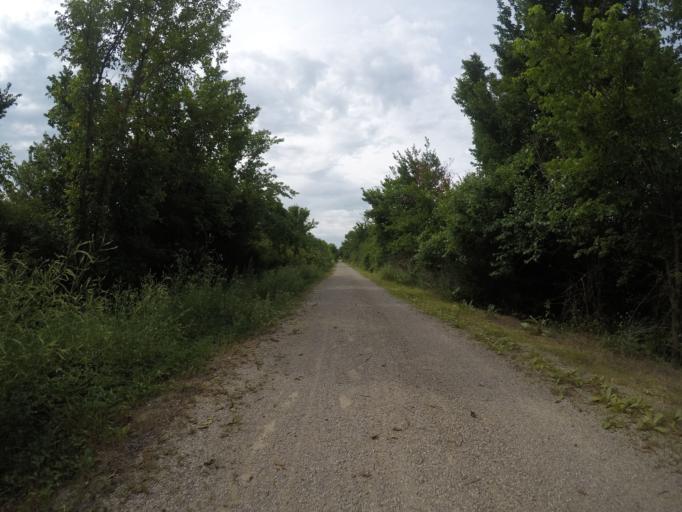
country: US
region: Kansas
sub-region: Anderson County
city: Garnett
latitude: 38.4380
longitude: -95.2641
